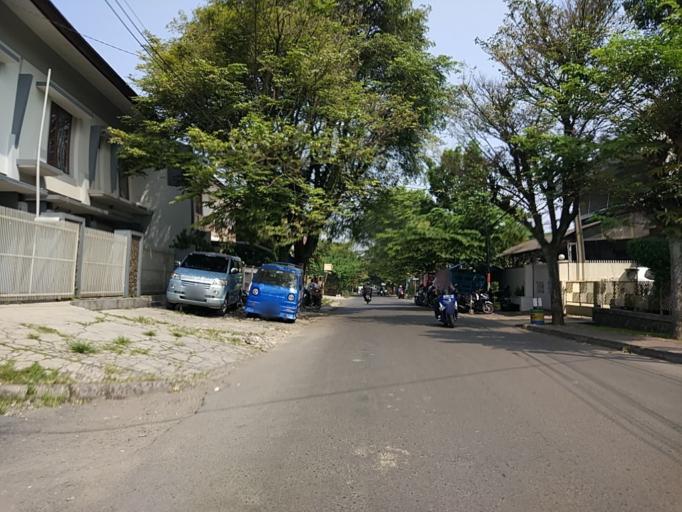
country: ID
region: West Java
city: Margahayukencana
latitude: -6.9360
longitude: 107.5739
